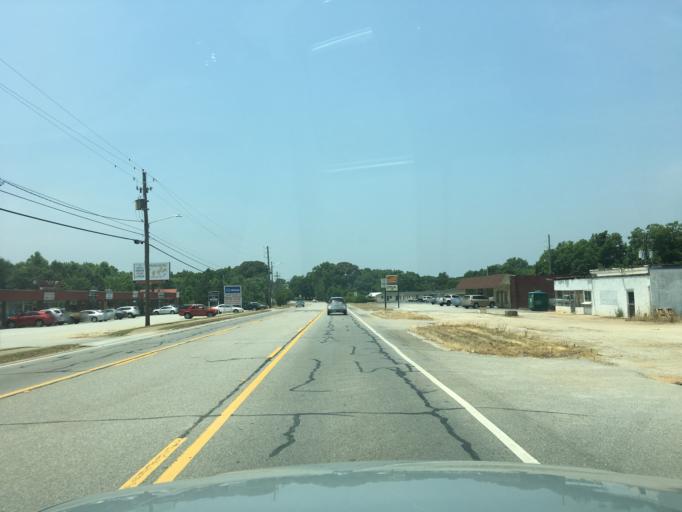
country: US
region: Georgia
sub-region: Hart County
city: Royston
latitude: 34.2853
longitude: -83.1285
